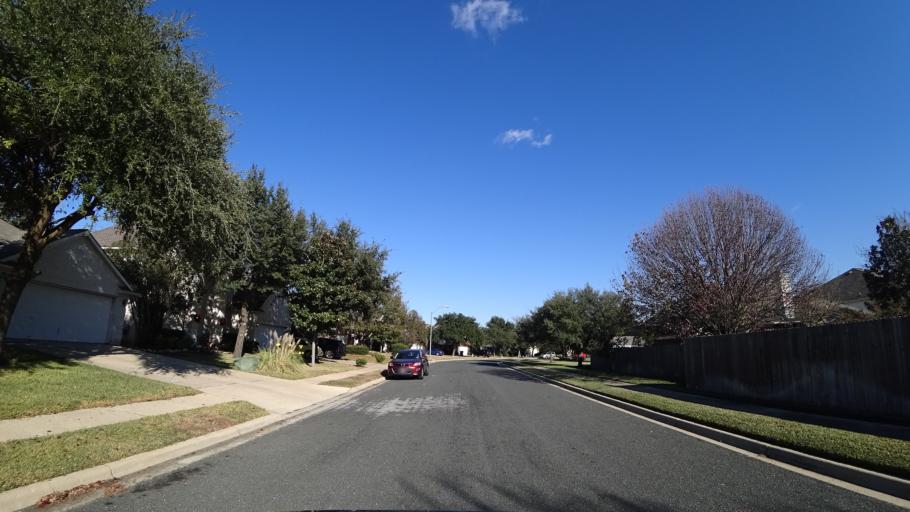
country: US
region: Texas
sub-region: Williamson County
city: Brushy Creek
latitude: 30.4898
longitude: -97.7366
